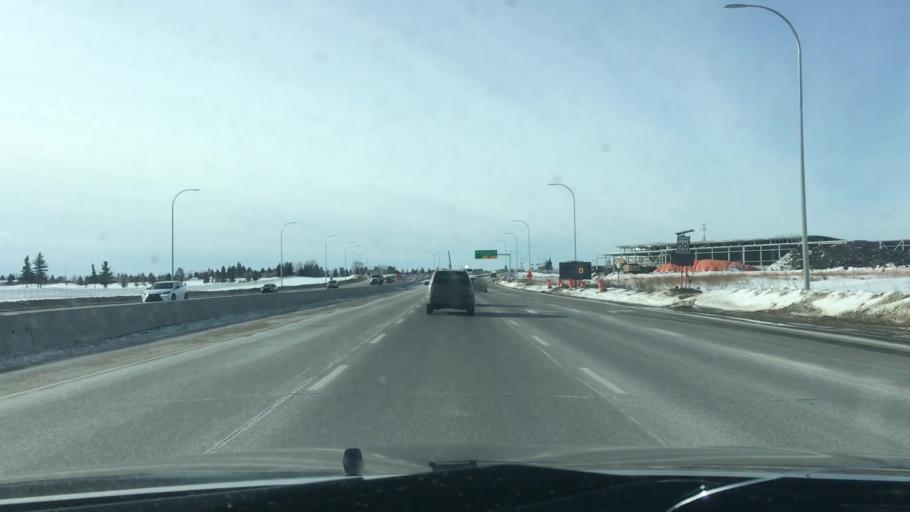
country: CA
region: Alberta
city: Edmonton
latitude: 53.4861
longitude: -113.4322
